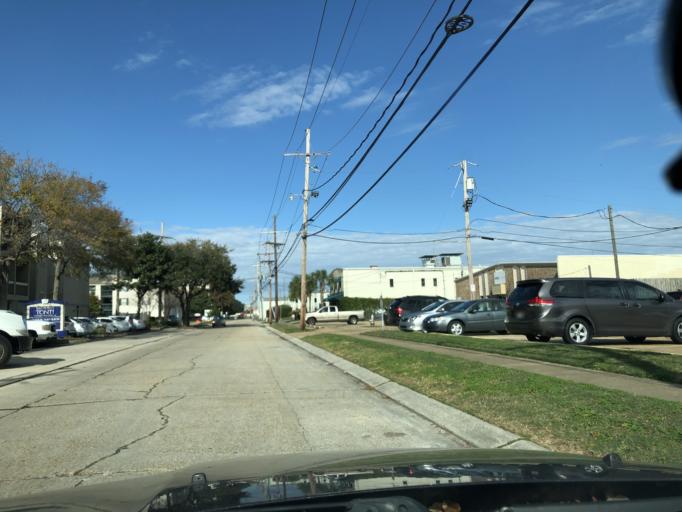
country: US
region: Louisiana
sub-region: Jefferson Parish
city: Metairie
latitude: 29.9943
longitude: -90.1624
